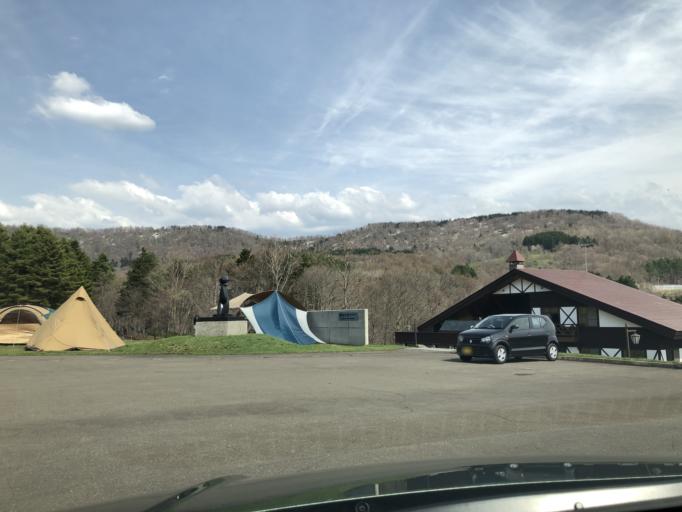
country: JP
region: Hokkaido
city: Akabira
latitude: 43.5947
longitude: 142.0467
